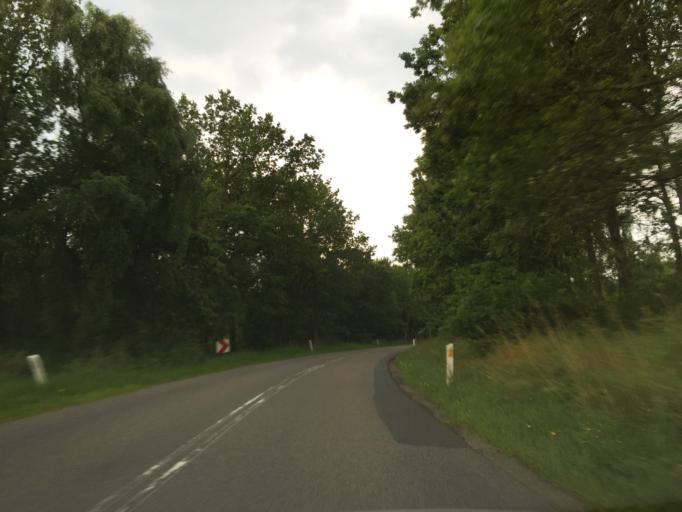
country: DK
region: Central Jutland
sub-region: Viborg Kommune
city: Bjerringbro
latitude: 56.3200
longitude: 9.6226
